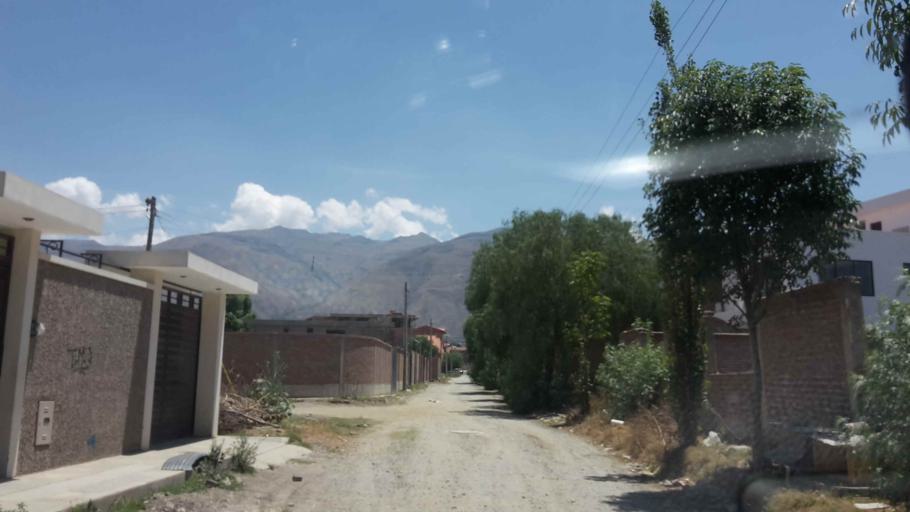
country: BO
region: Cochabamba
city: Cochabamba
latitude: -17.3713
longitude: -66.1941
